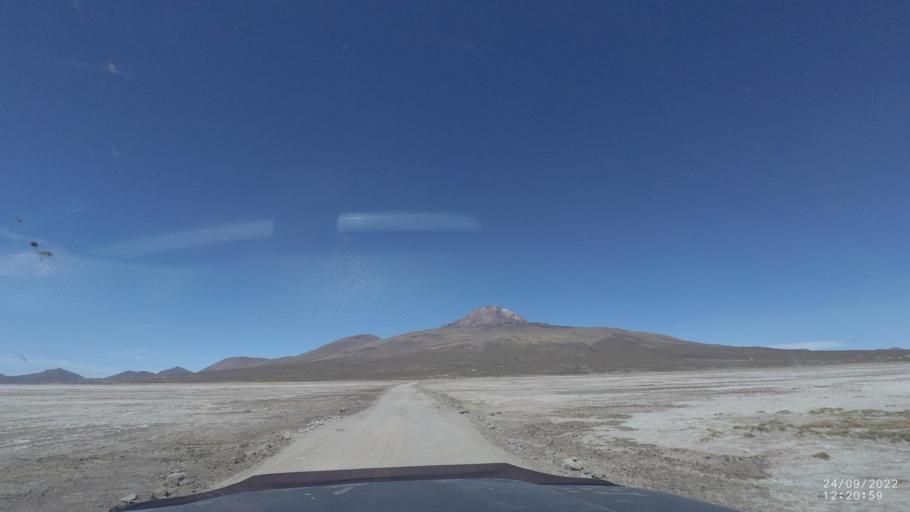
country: BO
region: Potosi
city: Colchani
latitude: -19.7460
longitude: -67.6703
